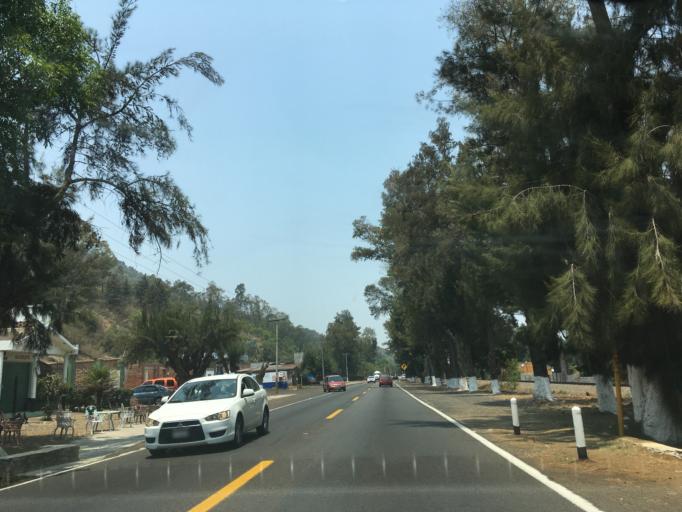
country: MX
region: Michoacan
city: Patzcuaro
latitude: 19.5463
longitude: -101.5970
